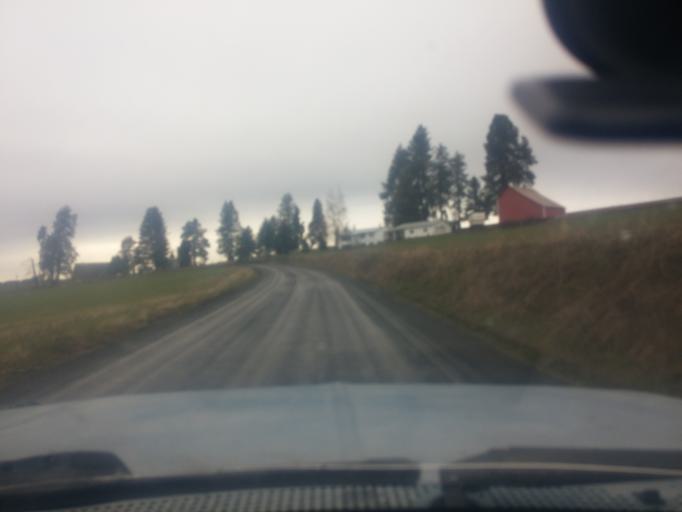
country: US
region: Idaho
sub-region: Latah County
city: Moscow
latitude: 46.9163
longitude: -116.8512
